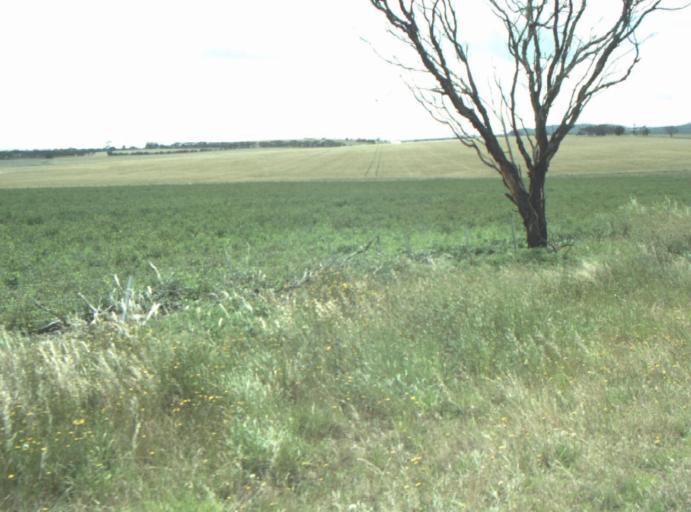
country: AU
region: Victoria
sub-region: Greater Geelong
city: Lara
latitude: -37.8907
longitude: 144.3482
